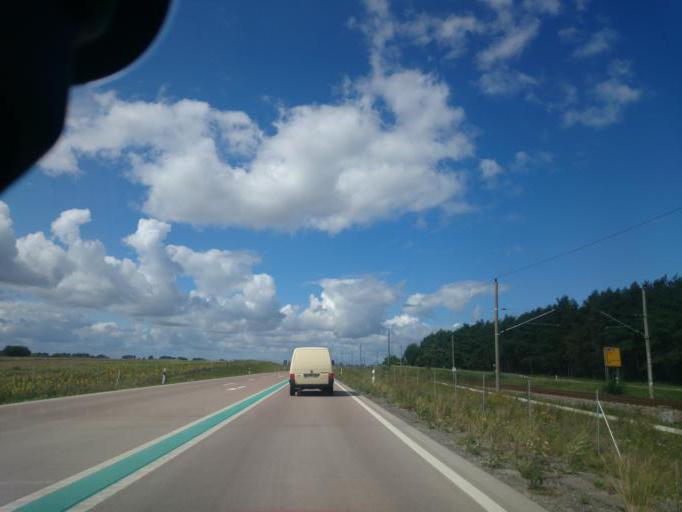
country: DE
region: Mecklenburg-Vorpommern
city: Rambin
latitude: 54.3543
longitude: 13.2469
